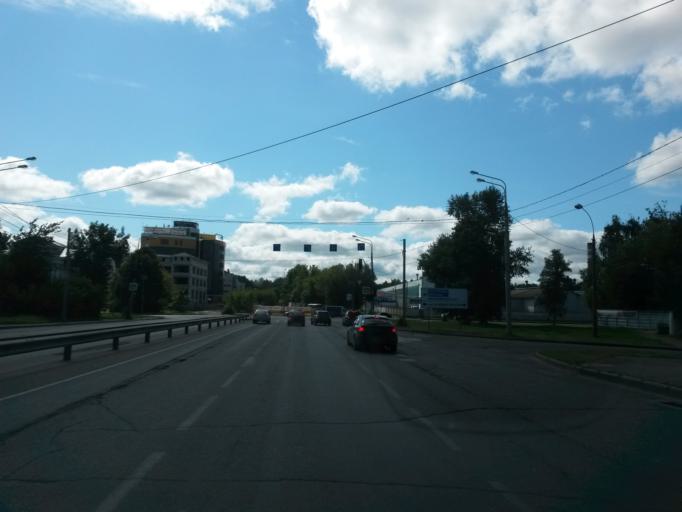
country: RU
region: Jaroslavl
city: Yaroslavl
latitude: 57.6096
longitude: 39.8600
